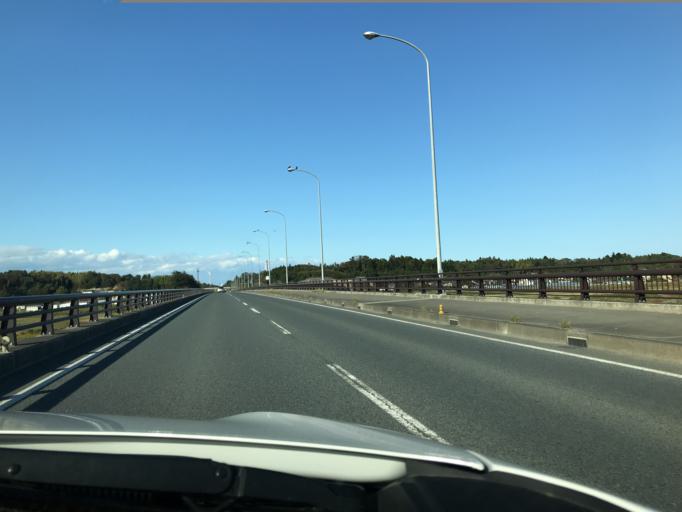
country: JP
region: Miyagi
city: Marumori
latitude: 37.8033
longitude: 140.9436
